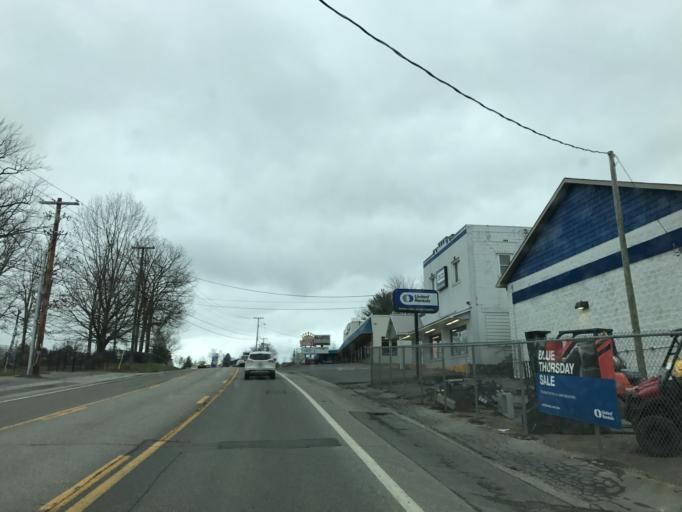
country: US
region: West Virginia
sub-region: Raleigh County
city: Beckley
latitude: 37.7873
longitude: -81.1721
